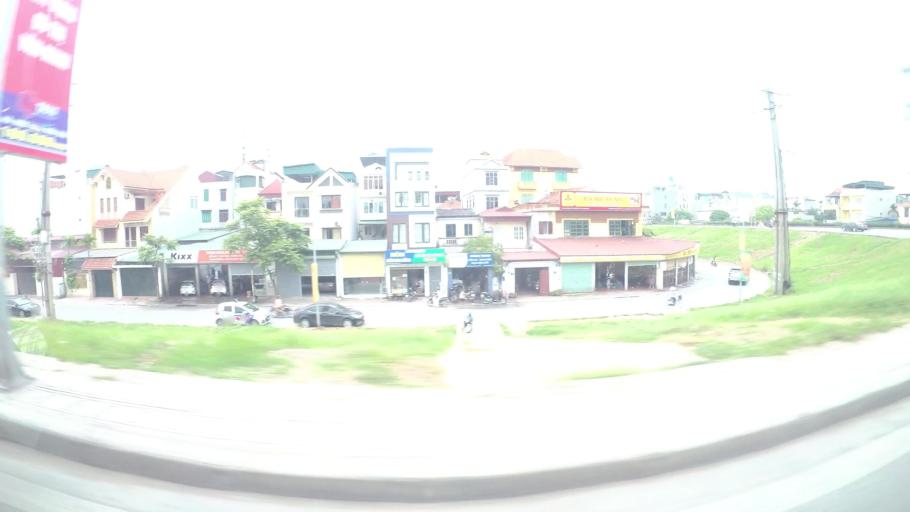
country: VN
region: Ha Noi
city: Hoan Kiem
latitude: 21.0619
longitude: 105.8629
